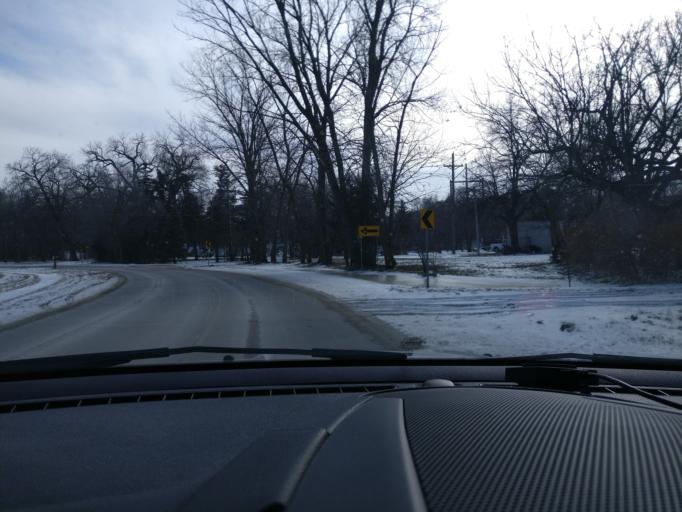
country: US
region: Nebraska
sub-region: Dodge County
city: Fremont
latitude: 41.4140
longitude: -96.5216
